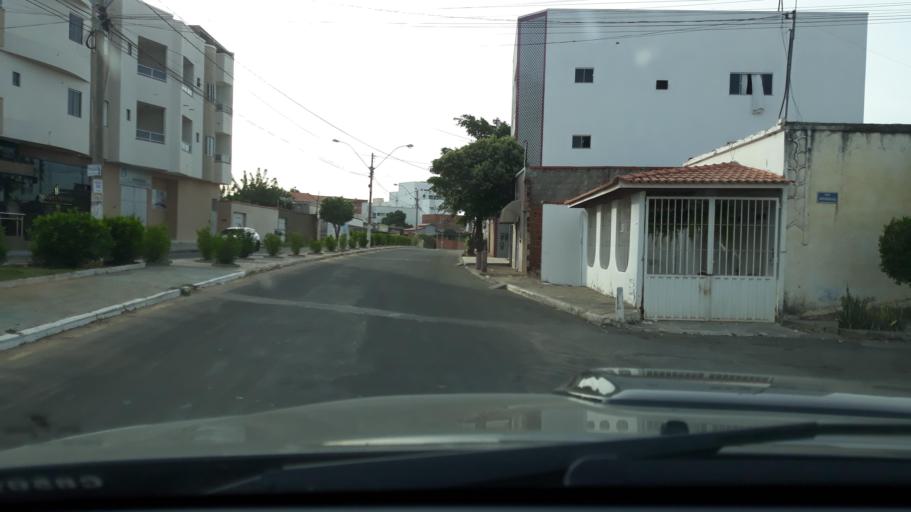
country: BR
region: Bahia
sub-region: Guanambi
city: Guanambi
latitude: -14.2315
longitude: -42.7789
